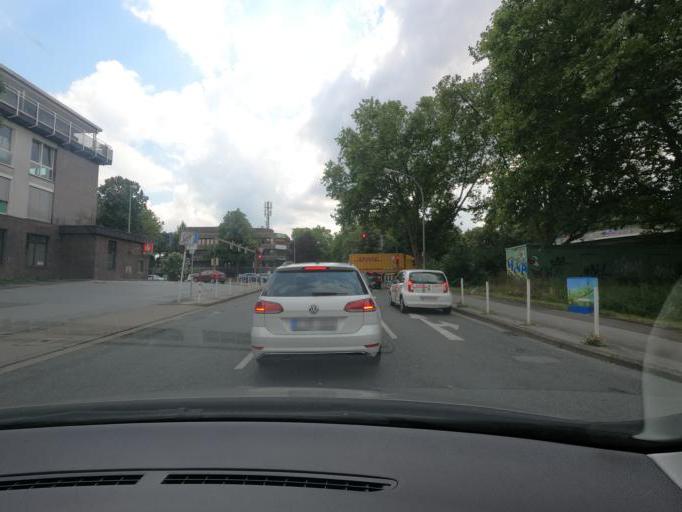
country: DE
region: North Rhine-Westphalia
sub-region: Regierungsbezirk Arnsberg
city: Dortmund
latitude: 51.5044
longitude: 7.5077
